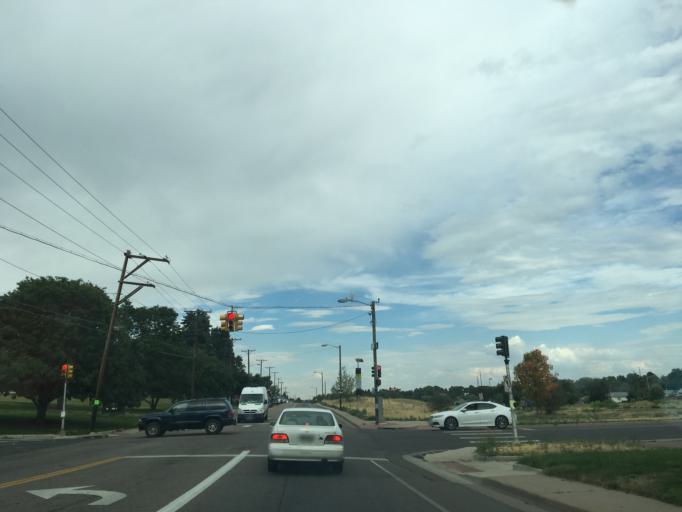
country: US
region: Colorado
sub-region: Arapahoe County
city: Sheridan
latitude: 39.6895
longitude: -105.0162
